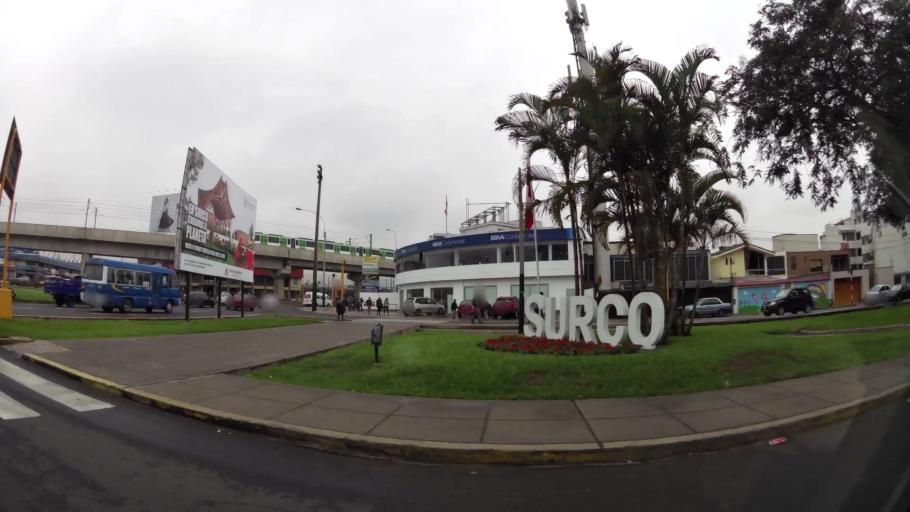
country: PE
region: Lima
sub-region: Lima
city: Surco
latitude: -12.1295
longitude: -77.0015
